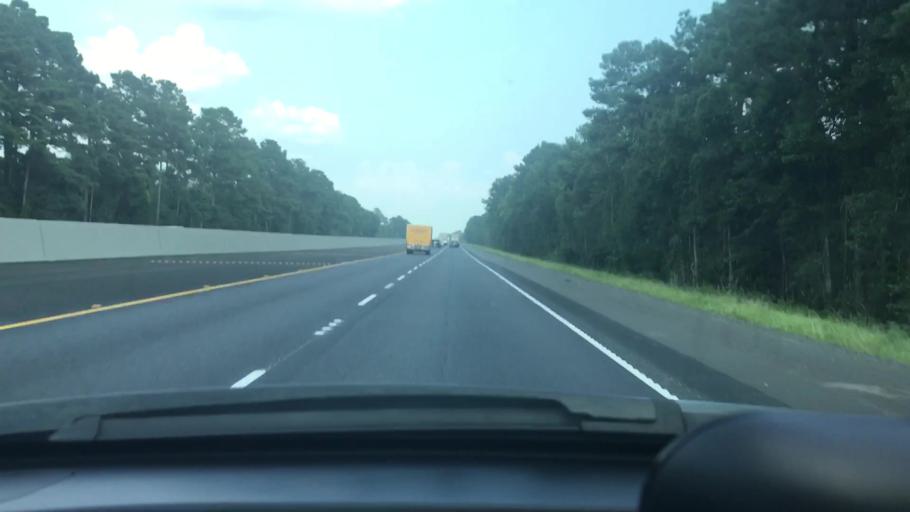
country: US
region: Louisiana
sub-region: Livingston Parish
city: Livingston
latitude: 30.4749
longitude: -90.6807
